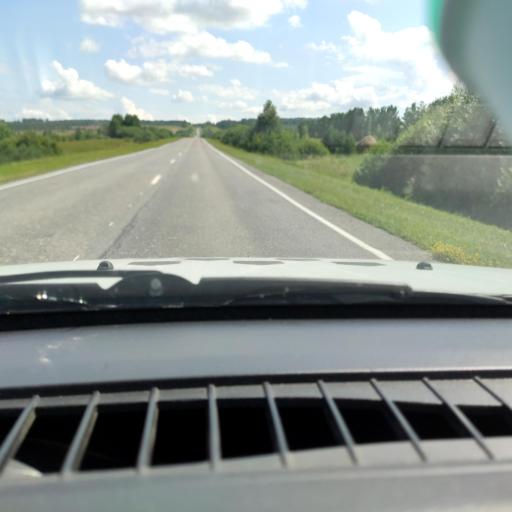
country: RU
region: Chelyabinsk
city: Mezhevoy
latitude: 55.3013
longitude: 58.7485
